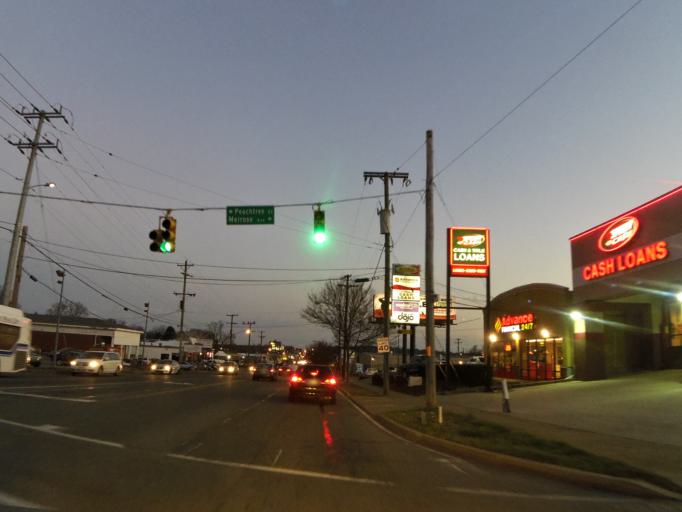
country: US
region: Tennessee
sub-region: Davidson County
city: Oak Hill
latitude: 36.1206
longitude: -86.7501
